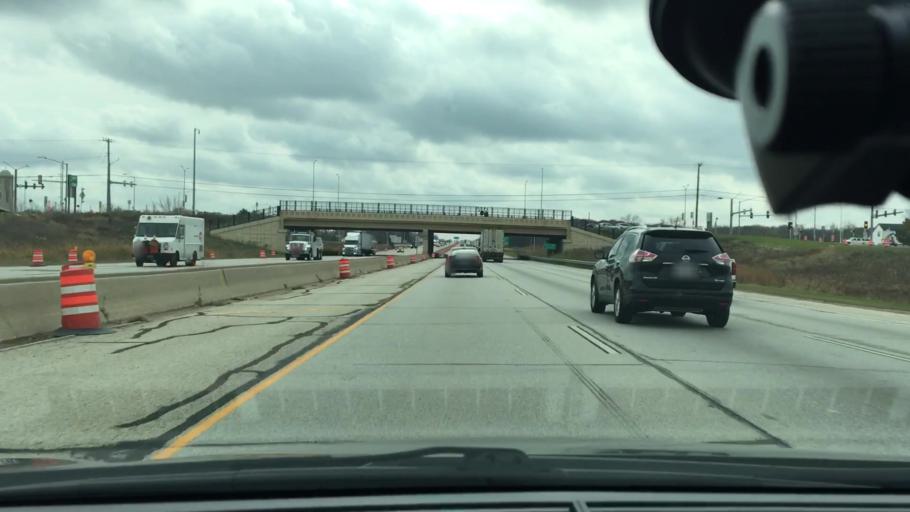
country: US
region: Wisconsin
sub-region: Milwaukee County
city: Greendale
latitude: 42.9032
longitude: -87.9363
